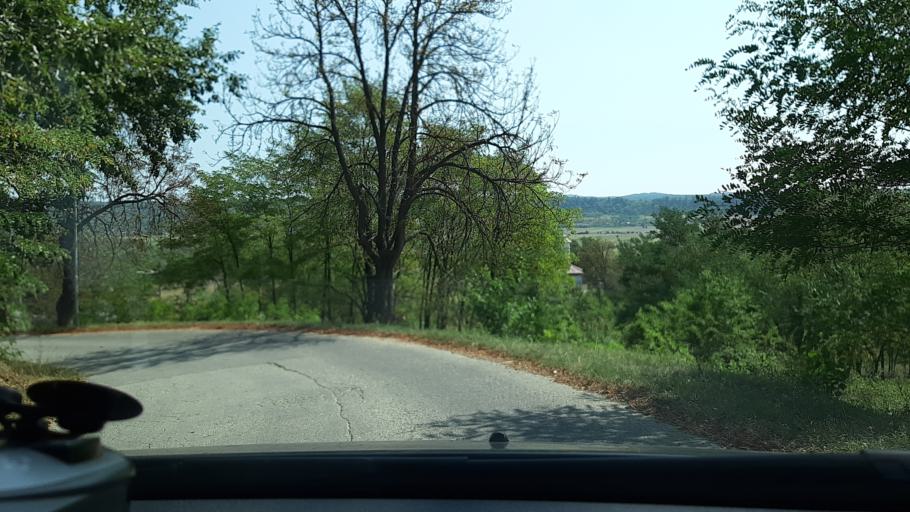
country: RO
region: Gorj
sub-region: Comuna Targu Carbunesti
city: Targu Carbunesti
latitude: 44.9629
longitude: 23.5195
